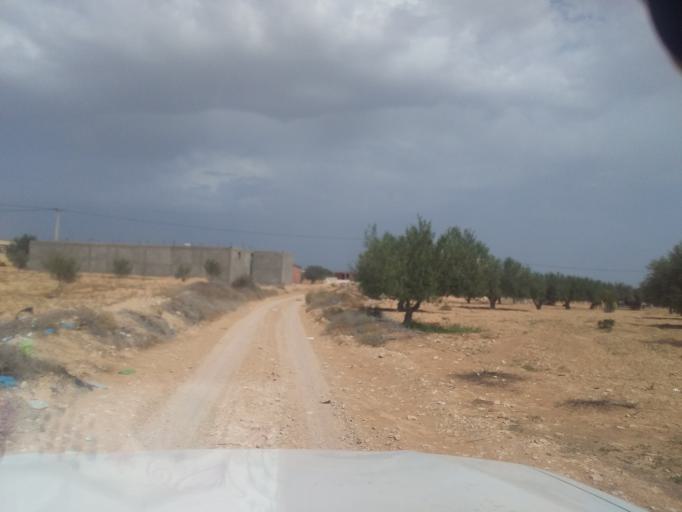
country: TN
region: Madanin
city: Medenine
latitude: 33.5905
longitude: 10.3252
